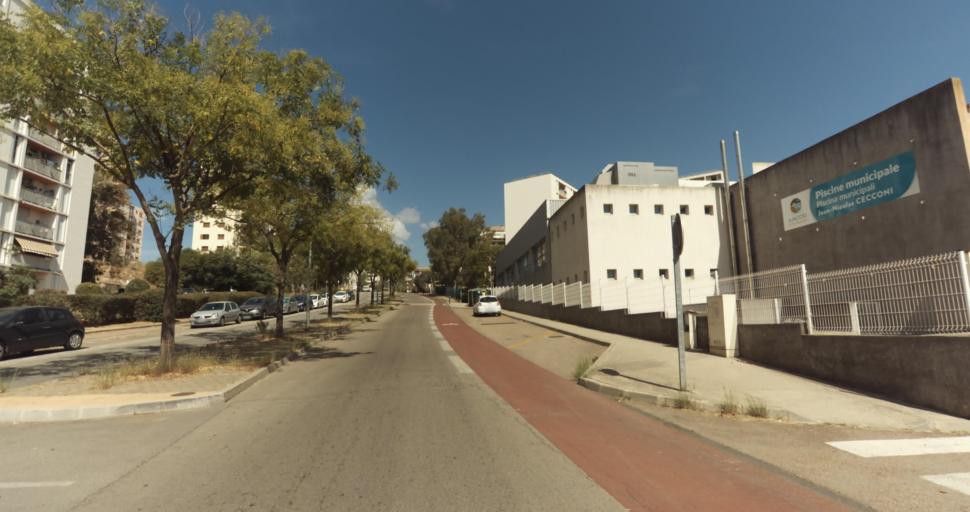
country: FR
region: Corsica
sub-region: Departement de la Corse-du-Sud
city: Ajaccio
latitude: 41.9378
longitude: 8.7510
